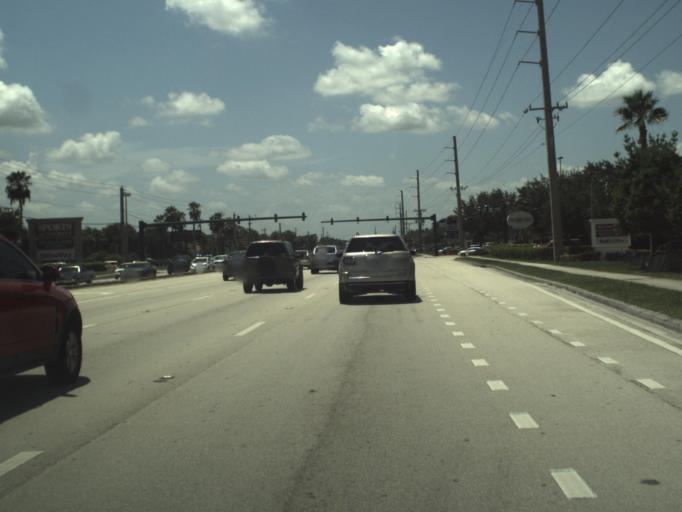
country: US
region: Florida
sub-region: Martin County
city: North River Shores
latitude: 27.2420
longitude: -80.2711
